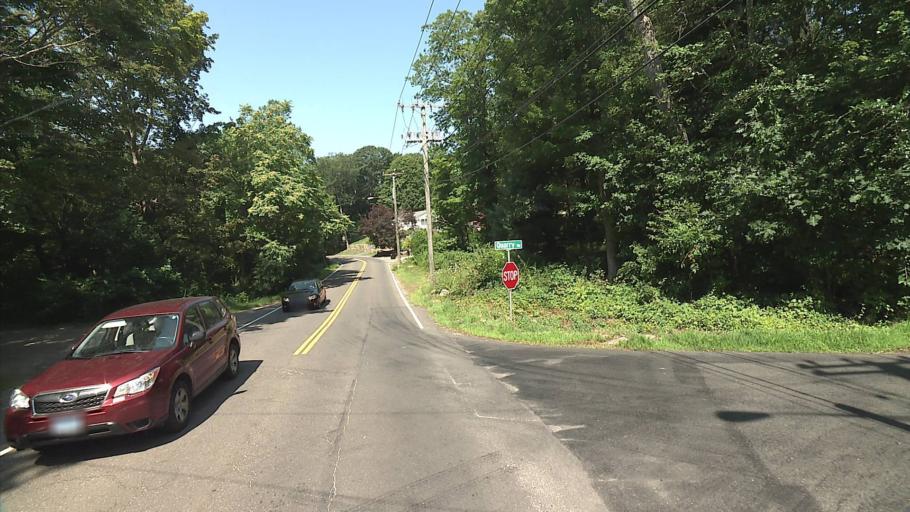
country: US
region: Connecticut
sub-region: New Haven County
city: North Branford
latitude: 41.2741
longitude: -72.7451
